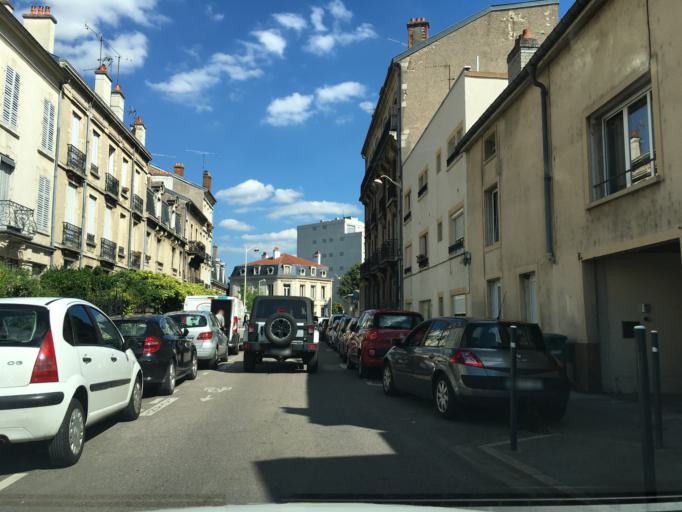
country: FR
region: Lorraine
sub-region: Departement de Meurthe-et-Moselle
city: Malzeville
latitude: 48.7021
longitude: 6.1780
